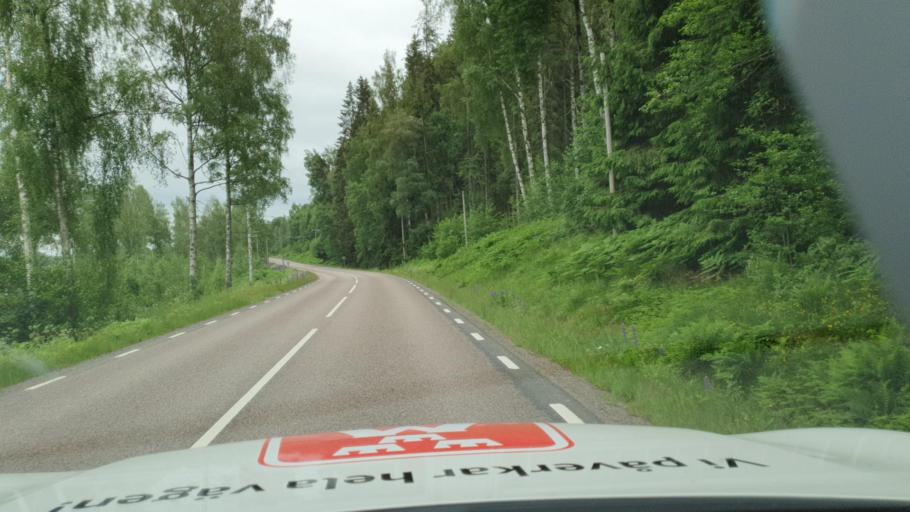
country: SE
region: Vaermland
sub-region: Sunne Kommun
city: Sunne
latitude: 59.8201
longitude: 13.0039
